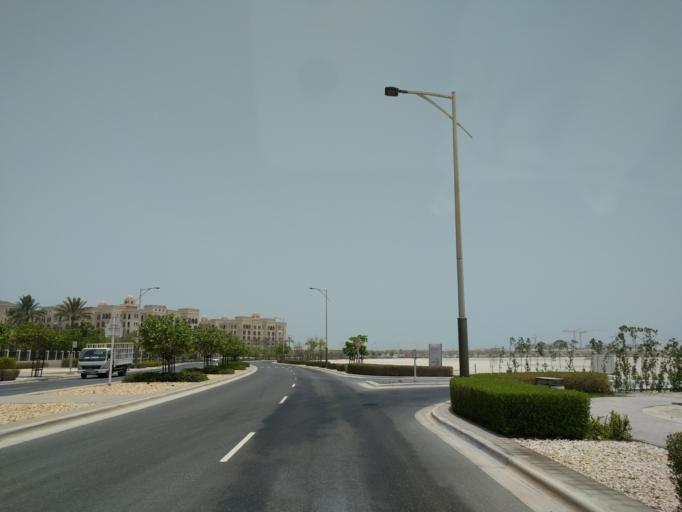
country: AE
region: Abu Dhabi
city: Abu Dhabi
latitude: 24.5505
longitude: 54.4545
